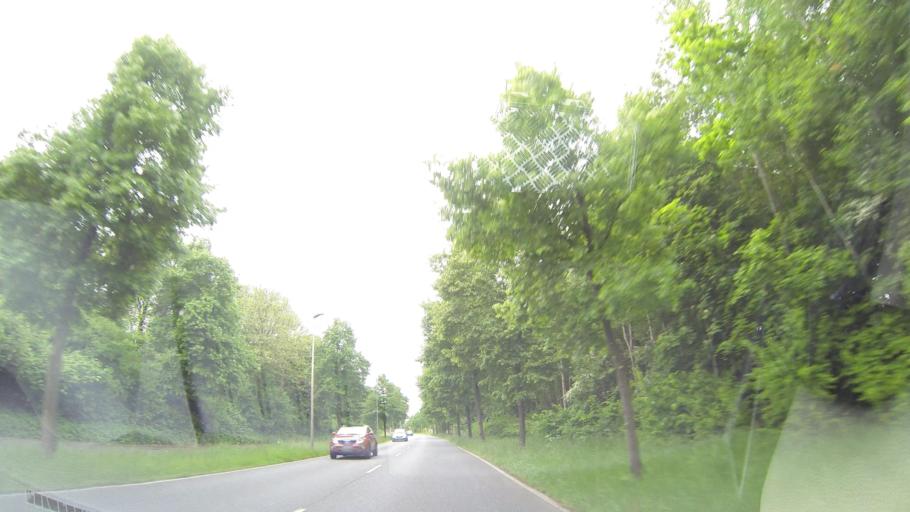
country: DE
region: Schleswig-Holstein
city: Halstenbek
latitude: 53.6180
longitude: 9.8546
